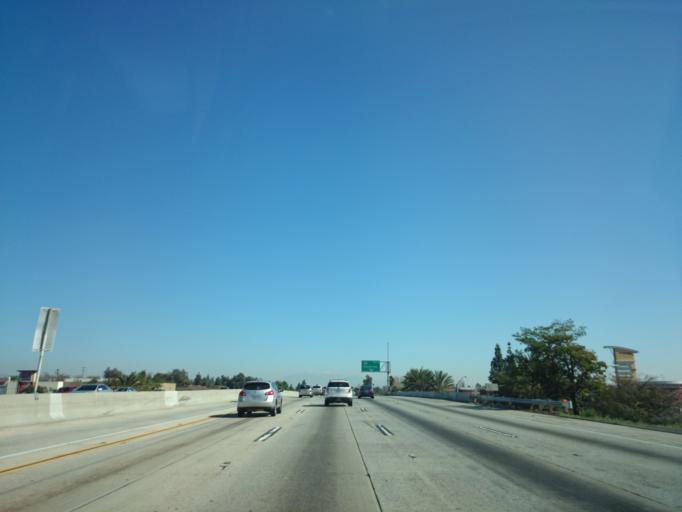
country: US
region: California
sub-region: San Bernardino County
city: Montclair
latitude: 34.0872
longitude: -117.6712
